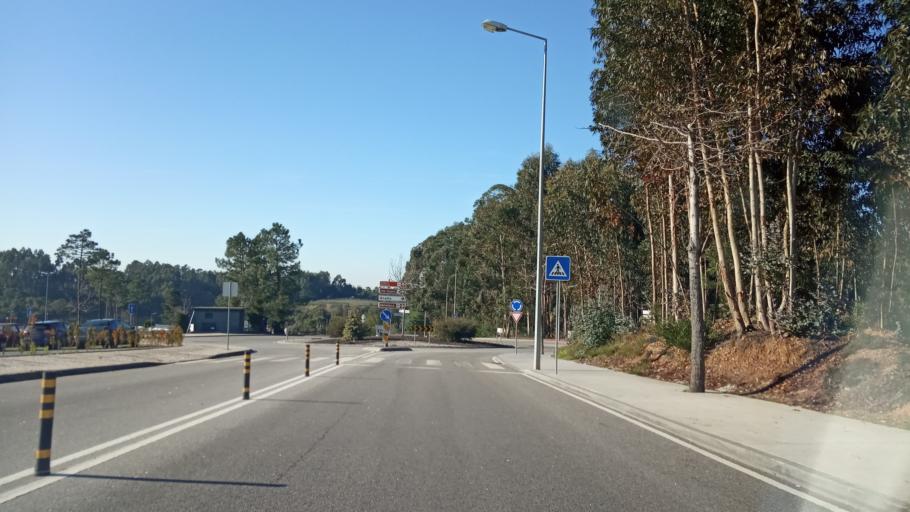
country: PT
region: Aveiro
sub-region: Anadia
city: Anadia
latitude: 40.4288
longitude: -8.4366
